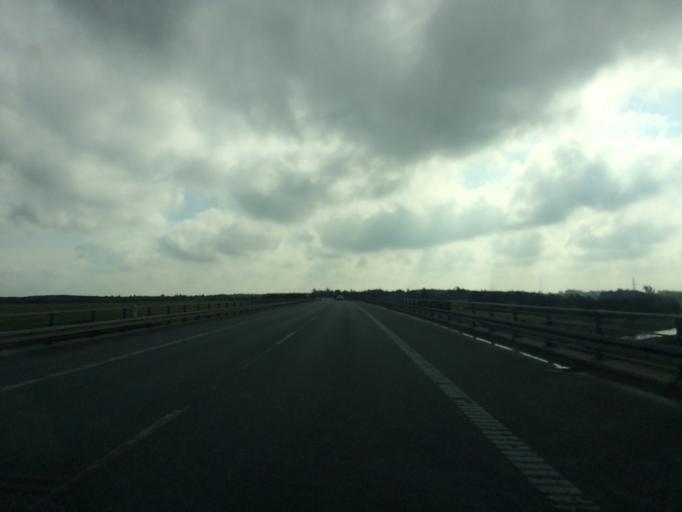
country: DK
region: Central Jutland
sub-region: Skive Kommune
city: Skive
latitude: 56.5451
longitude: 8.9960
